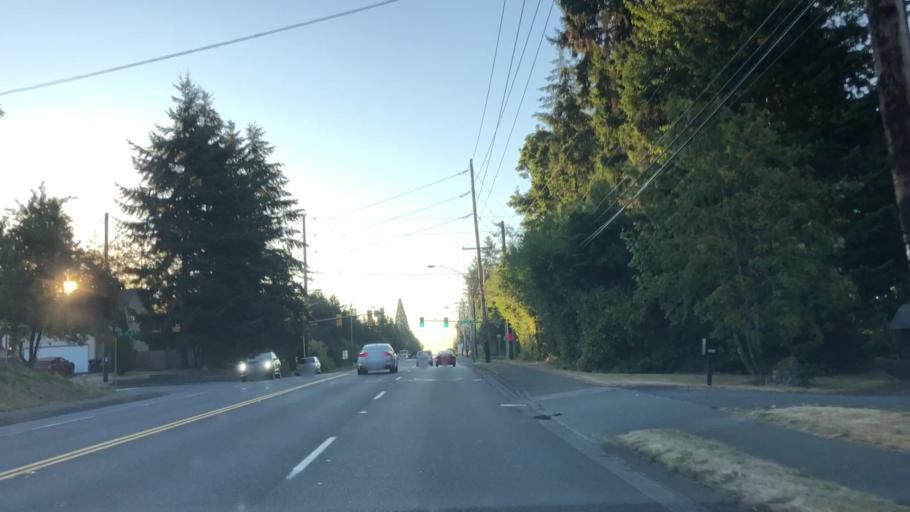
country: US
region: Washington
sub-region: King County
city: Lakeland North
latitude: 47.3578
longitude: -122.2825
